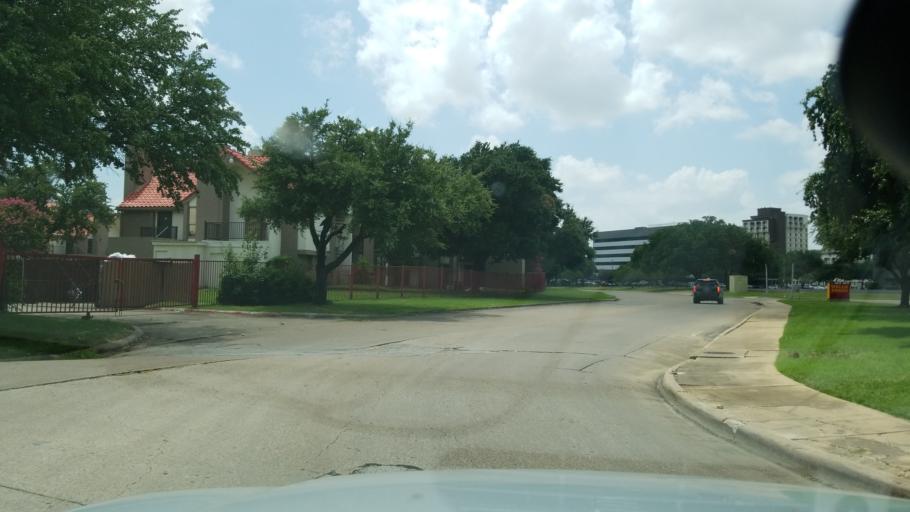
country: US
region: Texas
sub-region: Dallas County
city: Dallas
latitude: 32.8196
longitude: -96.8636
